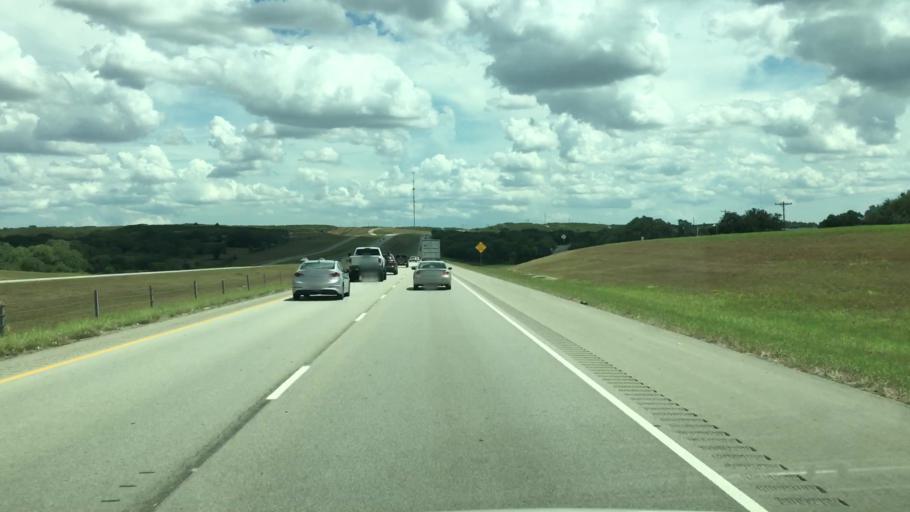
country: US
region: Texas
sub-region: Live Oak County
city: George West
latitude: 28.2640
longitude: -97.9343
